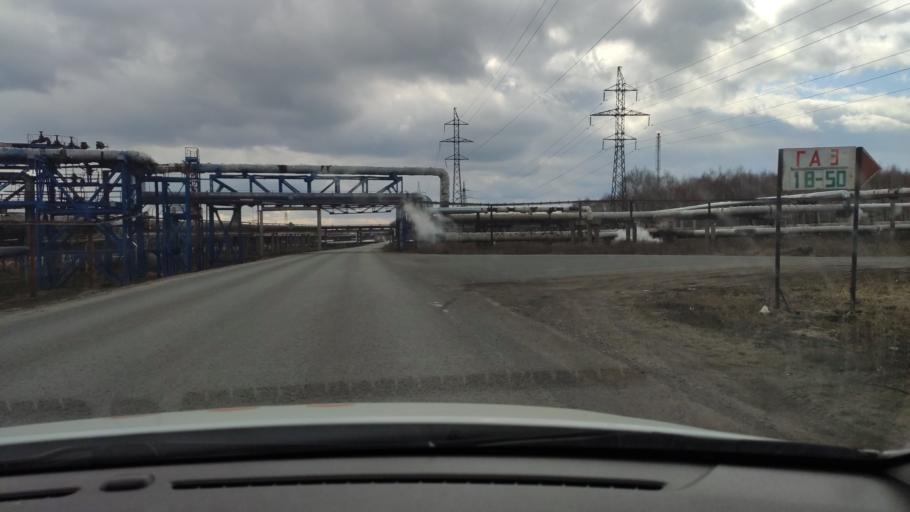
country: RU
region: Tatarstan
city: Staroye Arakchino
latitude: 55.8703
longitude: 48.9738
